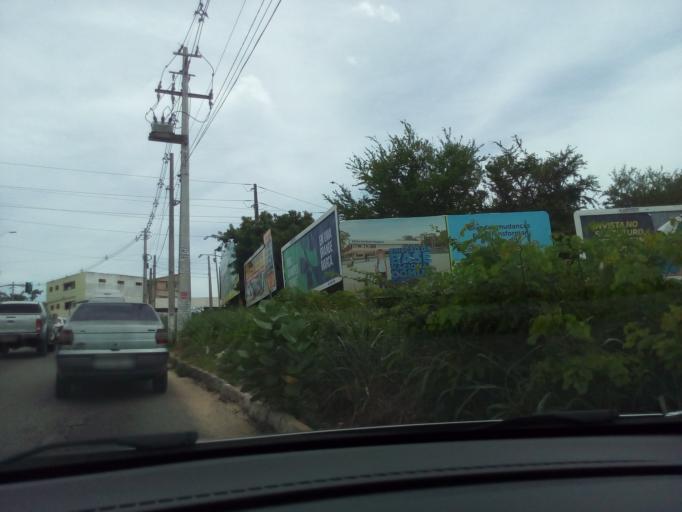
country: BR
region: Rio Grande do Norte
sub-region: Natal
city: Natal
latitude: -5.8419
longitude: -35.2217
